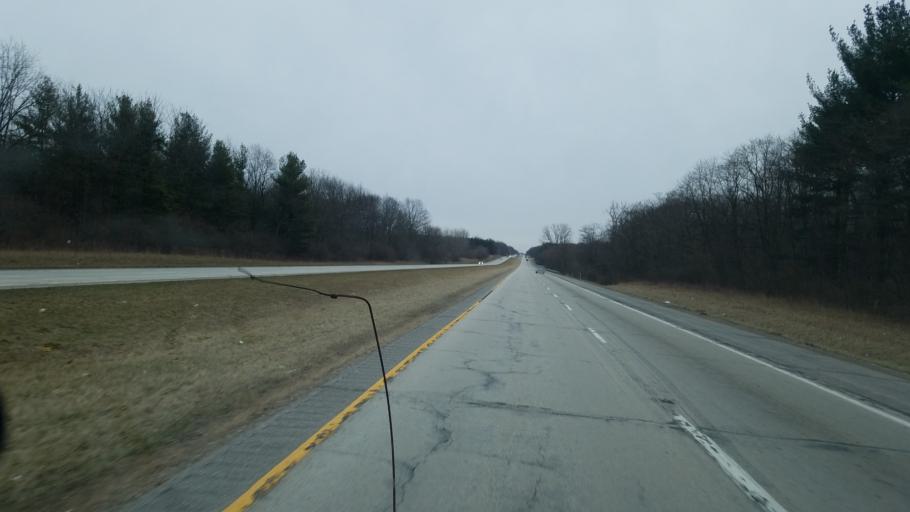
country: US
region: Indiana
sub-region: Starke County
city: Koontz Lake
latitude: 41.3645
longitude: -86.4555
